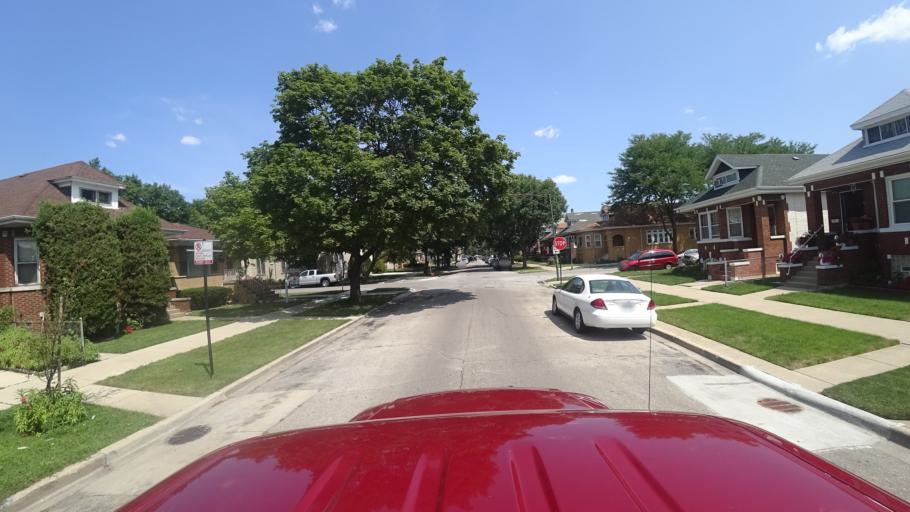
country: US
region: Illinois
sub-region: Cook County
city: Hometown
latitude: 41.7951
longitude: -87.6963
